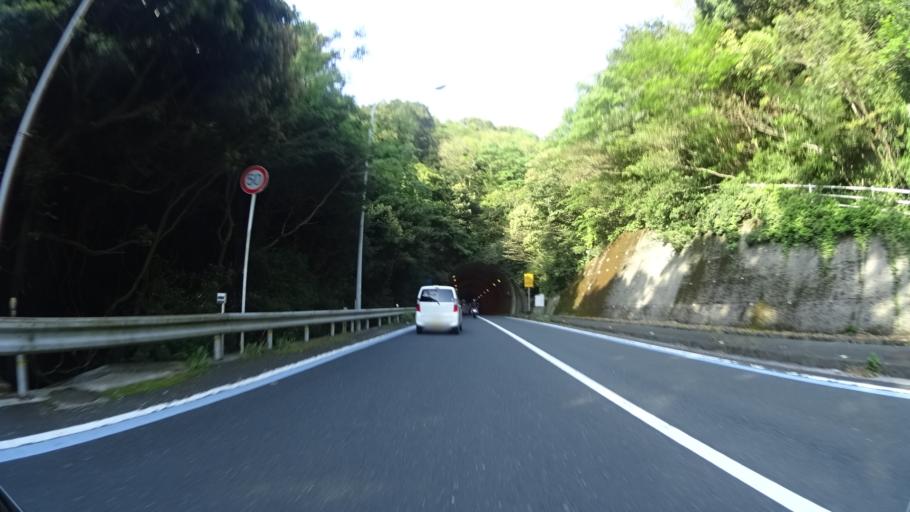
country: JP
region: Ehime
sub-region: Nishiuwa-gun
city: Ikata-cho
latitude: 33.4348
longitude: 132.2314
